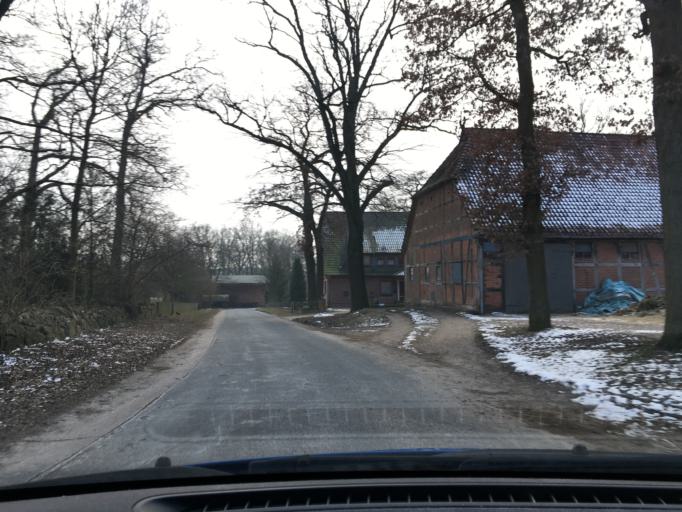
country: DE
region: Lower Saxony
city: Bienenbuttel
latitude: 53.1535
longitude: 10.4765
